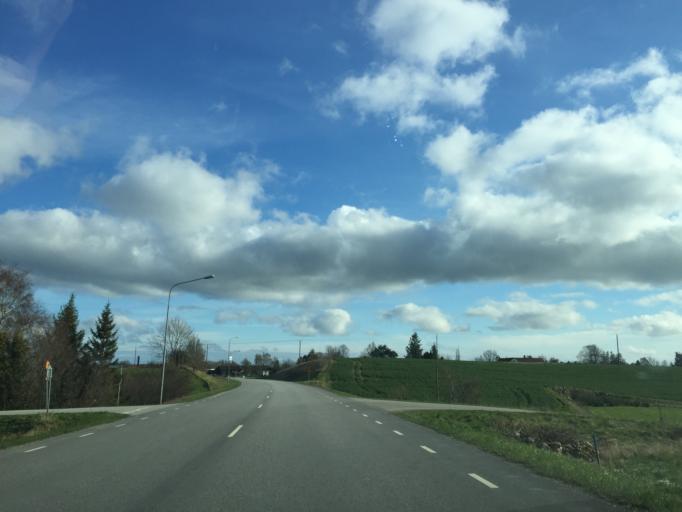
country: SE
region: Skane
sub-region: Skurups Kommun
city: Rydsgard
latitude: 55.4804
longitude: 13.5931
